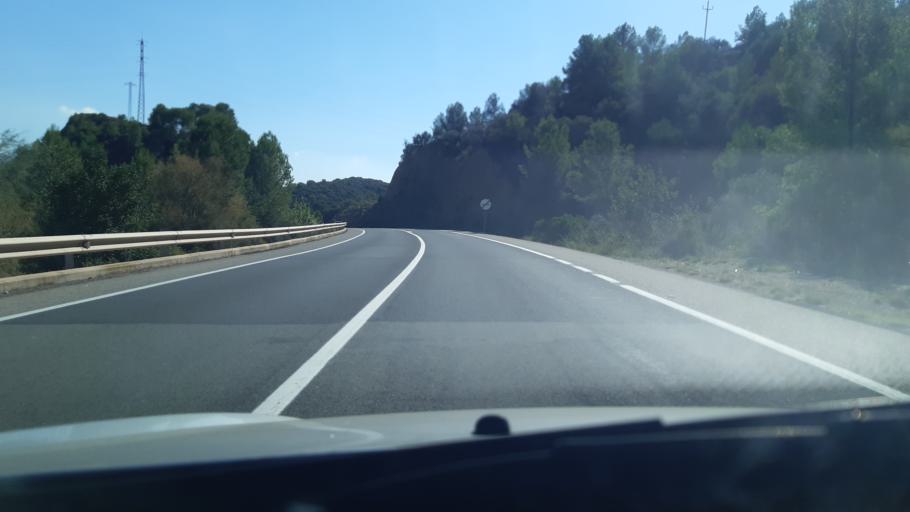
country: ES
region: Catalonia
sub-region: Provincia de Tarragona
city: Tivenys
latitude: 40.9266
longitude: 0.4866
